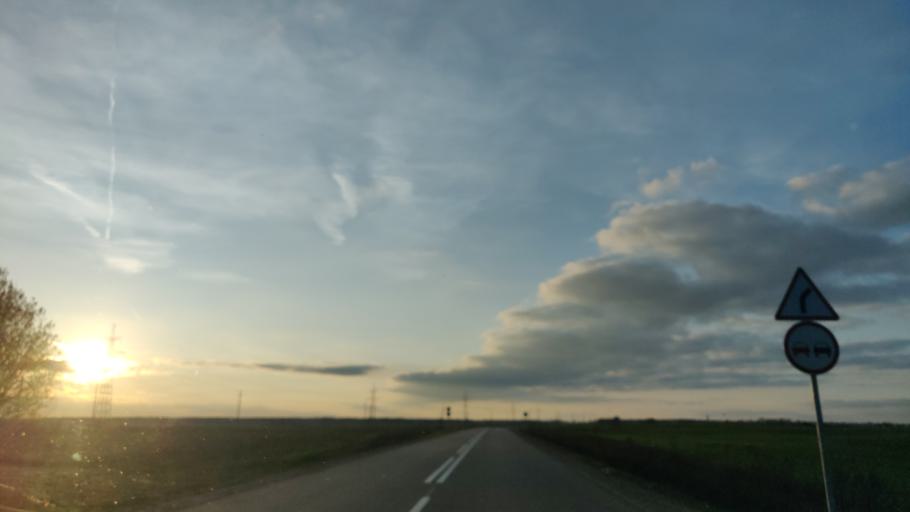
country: LT
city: Lentvaris
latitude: 54.6009
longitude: 25.0129
